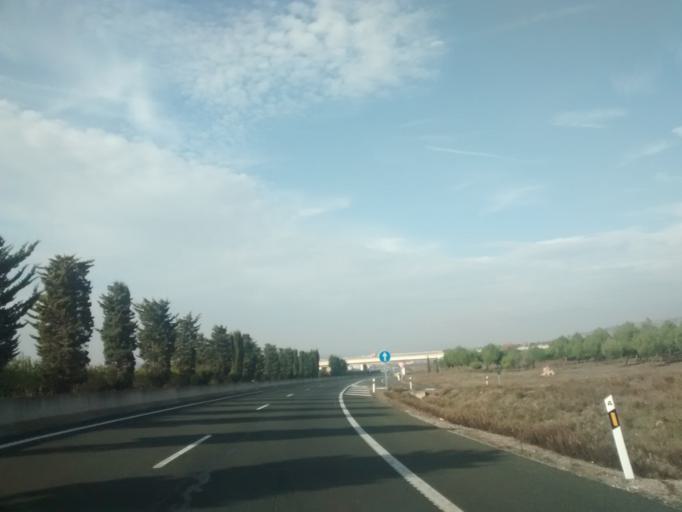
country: ES
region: La Rioja
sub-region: Provincia de La Rioja
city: Navarrete
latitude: 42.4413
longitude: -2.5430
